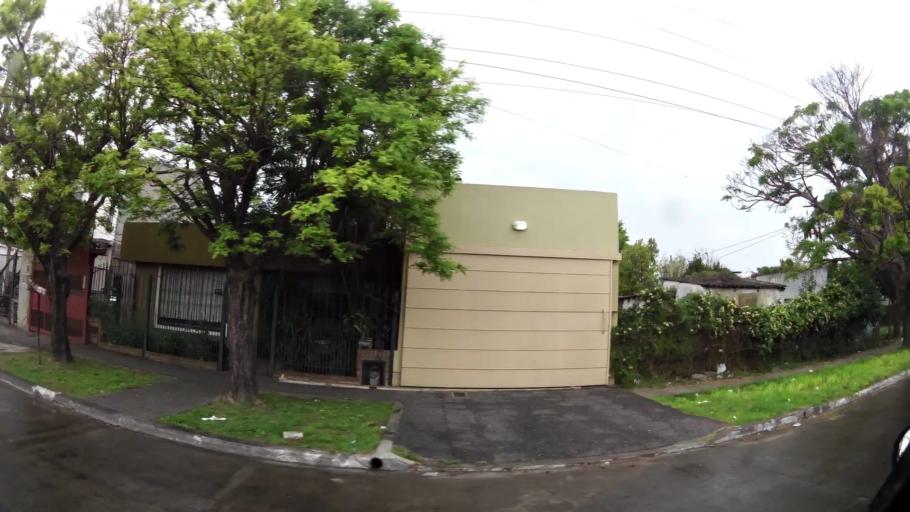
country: AR
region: Buenos Aires
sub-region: Partido de Quilmes
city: Quilmes
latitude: -34.7716
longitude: -58.2176
